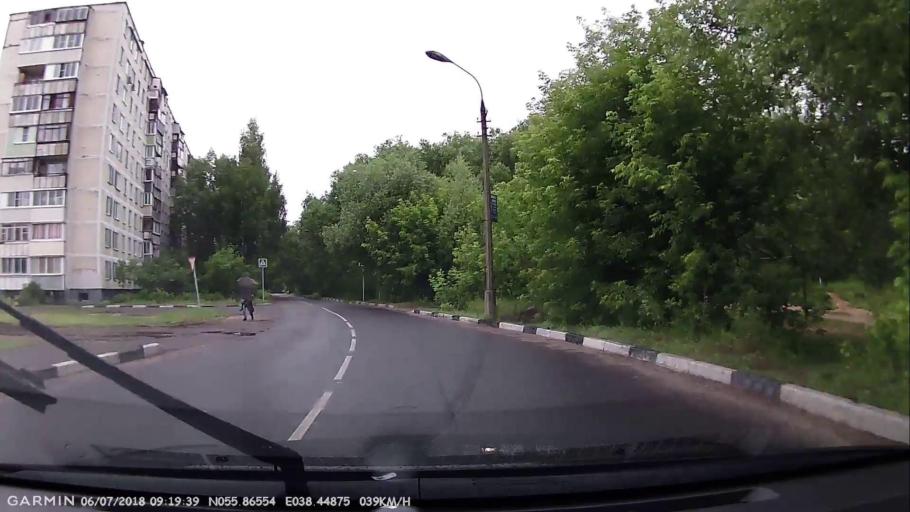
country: RU
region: Moskovskaya
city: Noginsk
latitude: 55.8657
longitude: 38.4488
